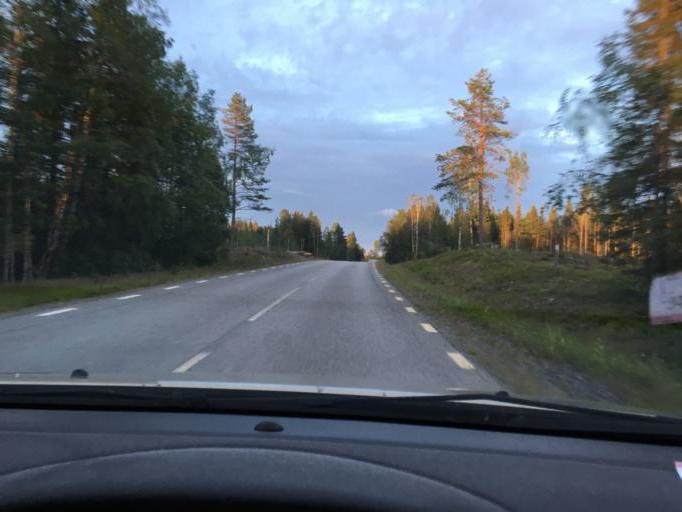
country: SE
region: Norrbotten
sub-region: Lulea Kommun
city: Ranea
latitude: 66.0521
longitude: 22.3838
